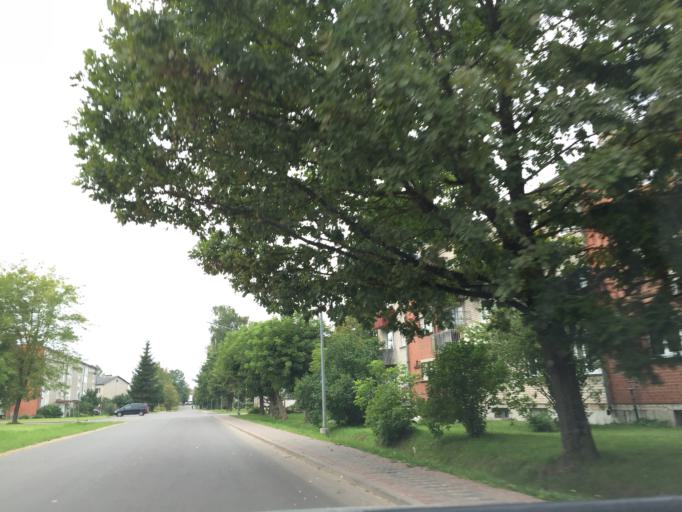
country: LV
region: Zilupes
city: Zilupe
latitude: 56.3888
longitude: 28.1280
